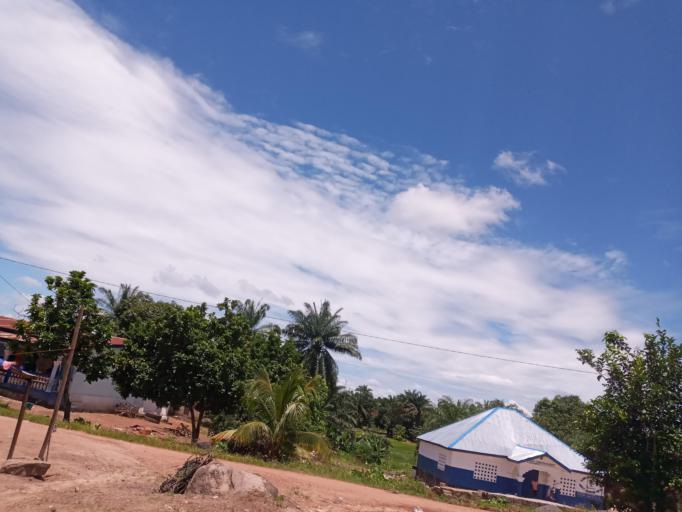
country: SL
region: Eastern Province
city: Koidu
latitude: 8.6424
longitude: -10.9630
